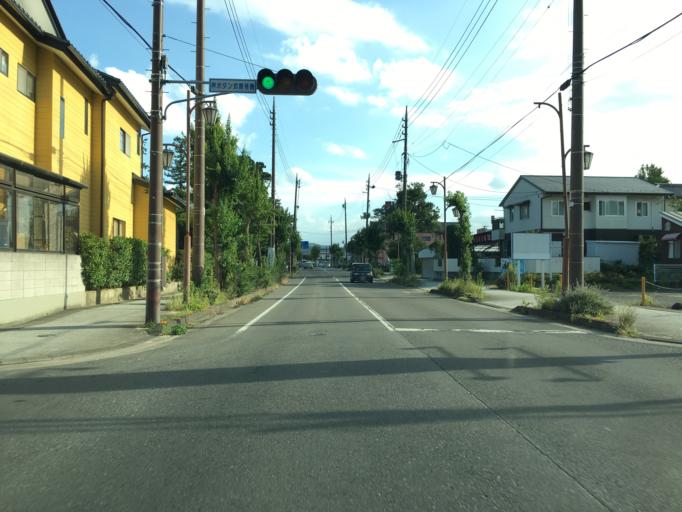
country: JP
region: Fukushima
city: Hobaramachi
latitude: 37.8221
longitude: 140.5578
